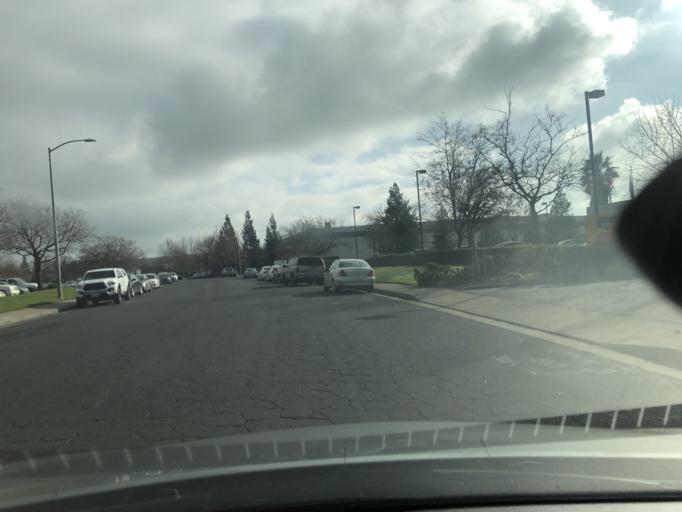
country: US
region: California
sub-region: Sacramento County
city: Rosemont
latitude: 38.5181
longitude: -121.3758
